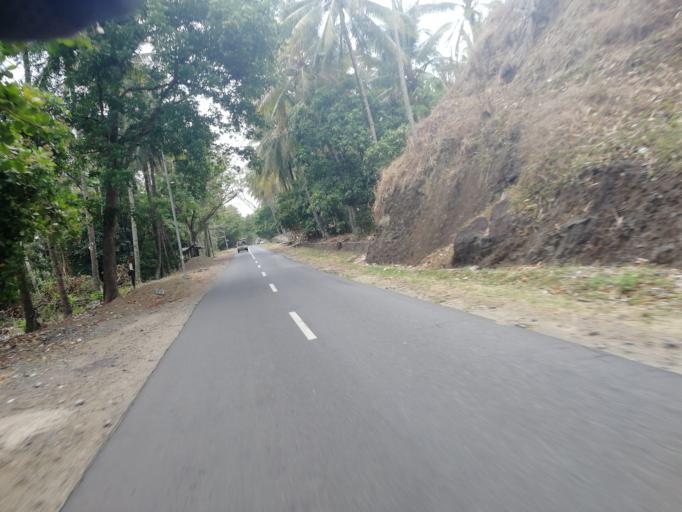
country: ID
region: West Nusa Tenggara
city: Karangsubagan
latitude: -8.4224
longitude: 116.0934
